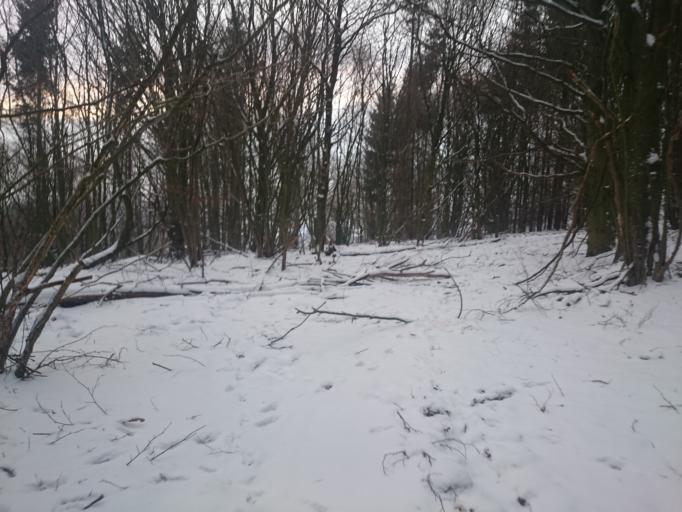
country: SE
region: Skane
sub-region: Sjobo Kommun
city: Sjoebo
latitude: 55.6019
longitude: 13.7603
